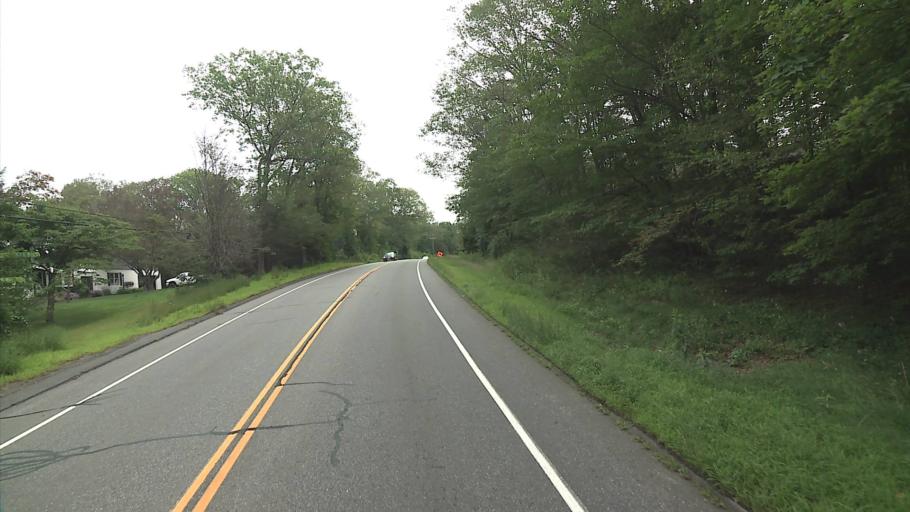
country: US
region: Connecticut
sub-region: Tolland County
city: Storrs
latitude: 41.8742
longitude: -72.2264
